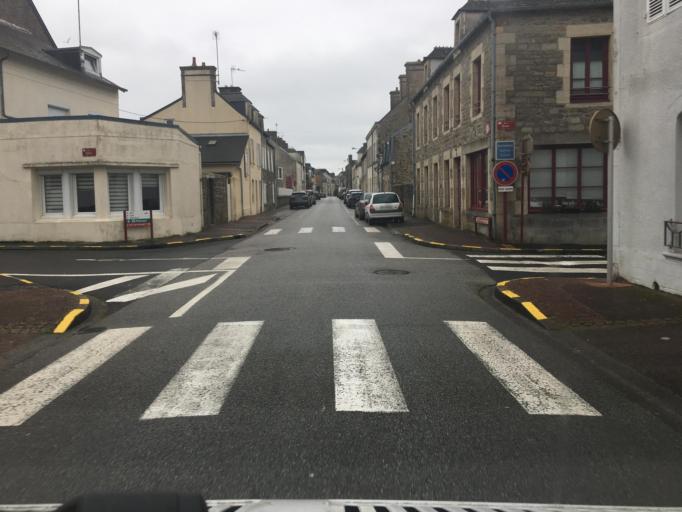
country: FR
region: Lower Normandy
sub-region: Departement de la Manche
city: Saint-Vaast-la-Hougue
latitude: 49.5869
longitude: -1.2687
